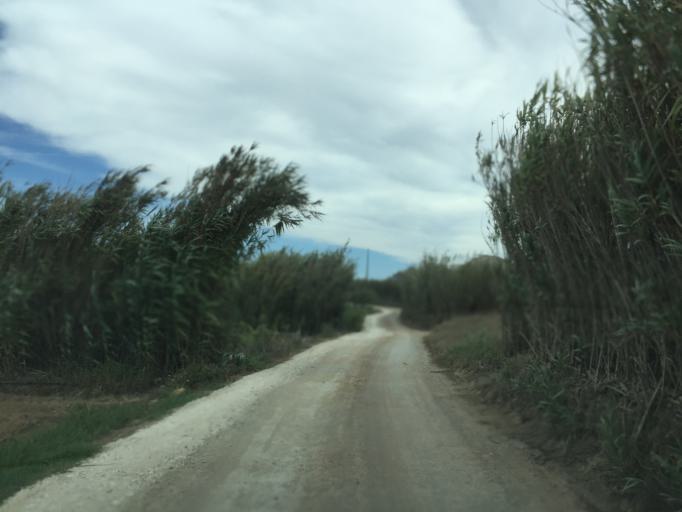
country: PT
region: Lisbon
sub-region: Lourinha
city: Lourinha
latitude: 39.1943
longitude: -9.3406
